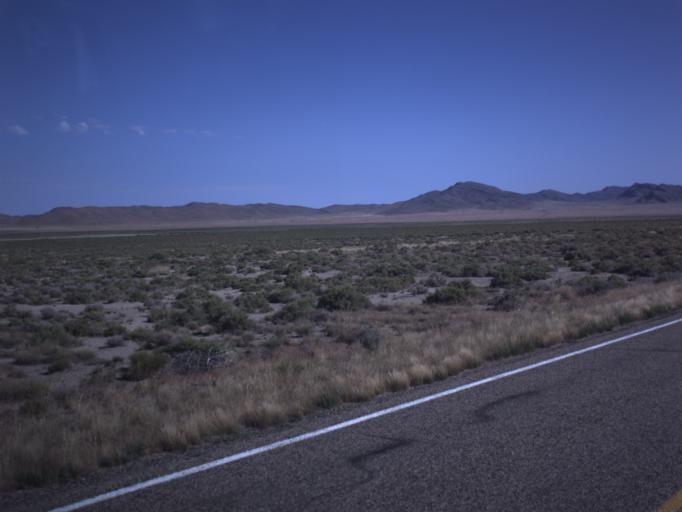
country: US
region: Utah
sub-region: Beaver County
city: Milford
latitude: 38.6757
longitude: -112.9794
